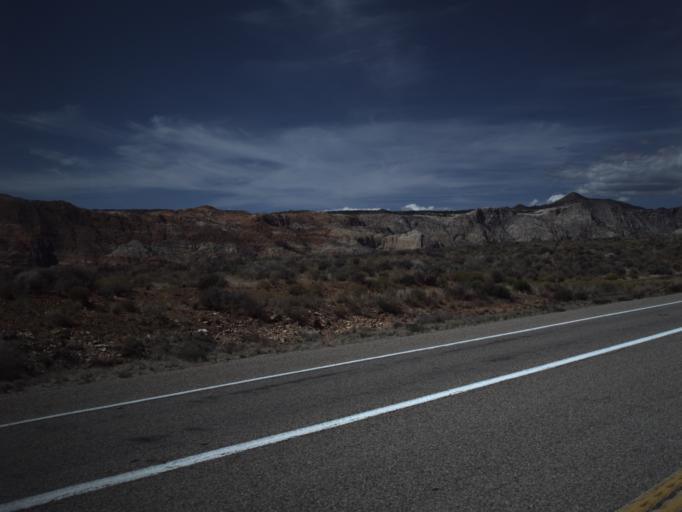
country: US
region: Utah
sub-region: Washington County
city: Ivins
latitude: 37.2085
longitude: -113.6290
